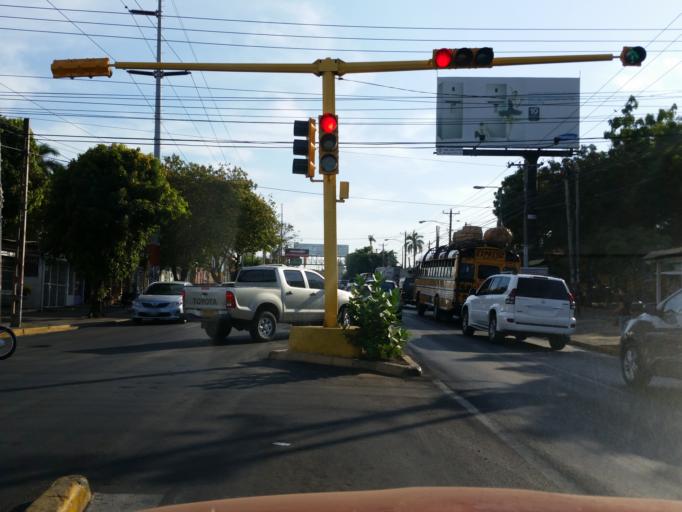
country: NI
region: Managua
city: Managua
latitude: 12.1158
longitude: -86.2526
